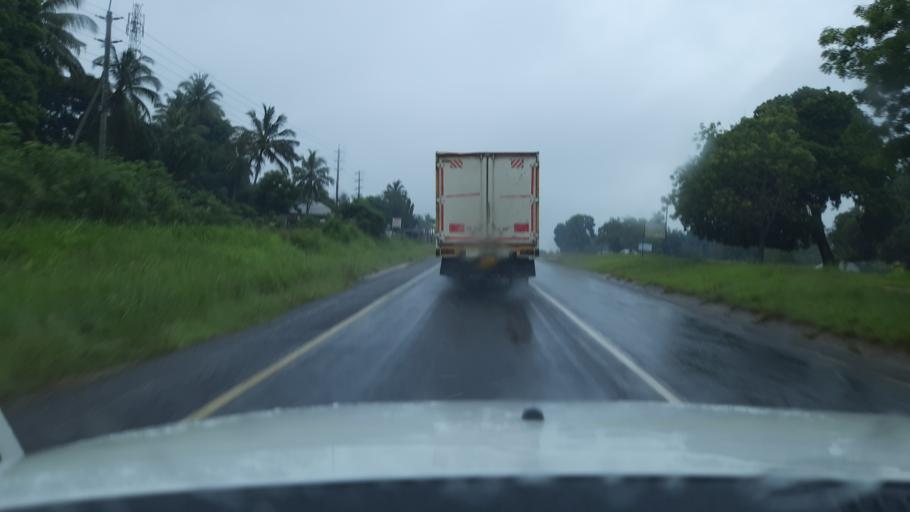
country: TZ
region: Pwani
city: Bagamoyo
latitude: -6.5818
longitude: 39.0341
